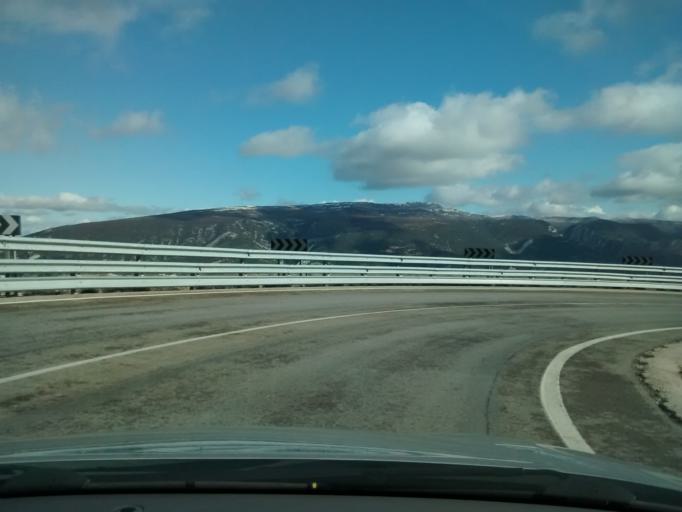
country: ES
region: Castille and Leon
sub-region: Provincia de Burgos
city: Rucandio
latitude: 42.8319
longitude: -3.6159
